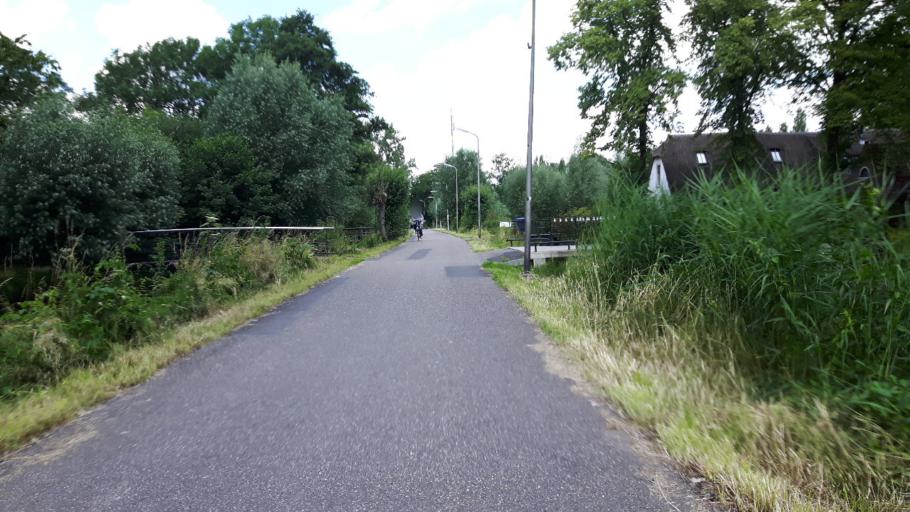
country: NL
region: South Holland
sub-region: Gemeente Gouda
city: Bloemendaal
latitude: 52.0324
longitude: 4.6955
